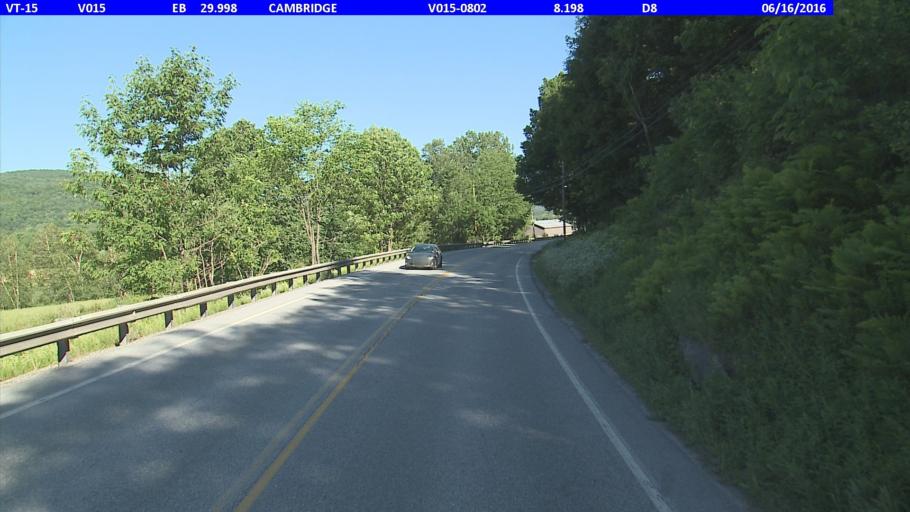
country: US
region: Vermont
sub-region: Lamoille County
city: Johnson
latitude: 44.6660
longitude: -72.7771
